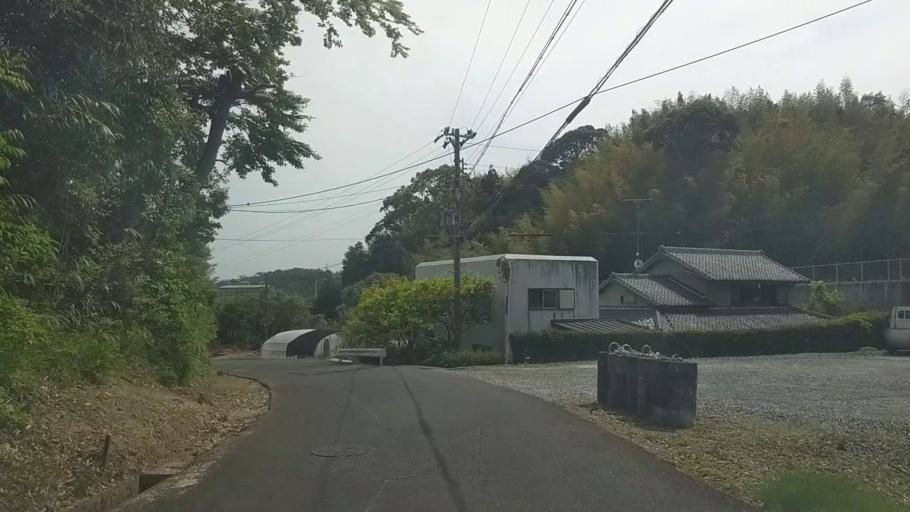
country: JP
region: Shizuoka
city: Kosai-shi
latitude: 34.7708
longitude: 137.6273
